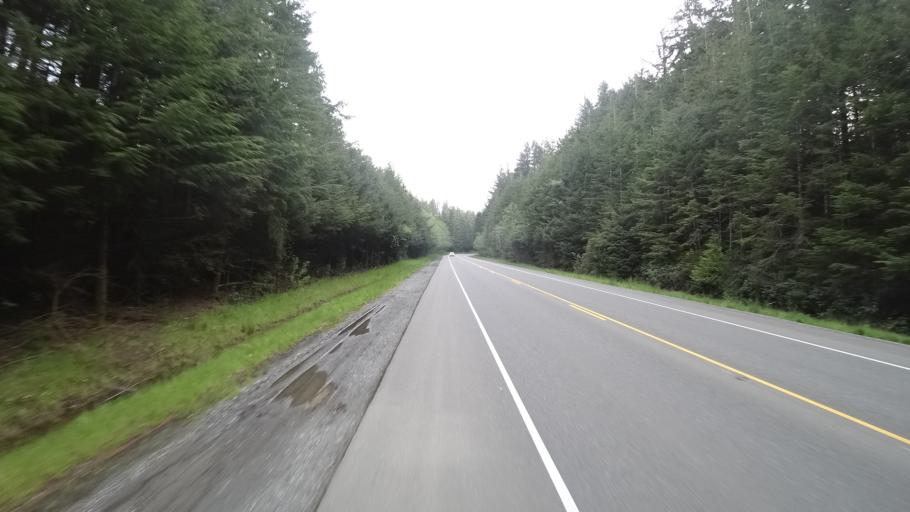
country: US
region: Oregon
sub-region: Coos County
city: Barview
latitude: 43.2514
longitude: -124.2864
